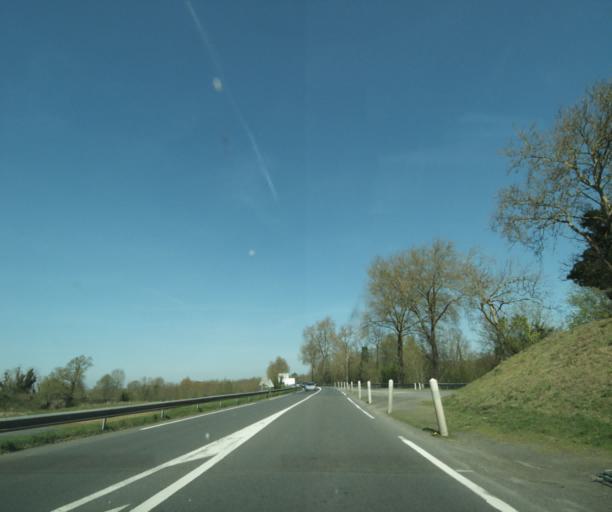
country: FR
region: Auvergne
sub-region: Departement de l'Allier
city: Trevol
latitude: 46.6257
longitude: 3.2858
